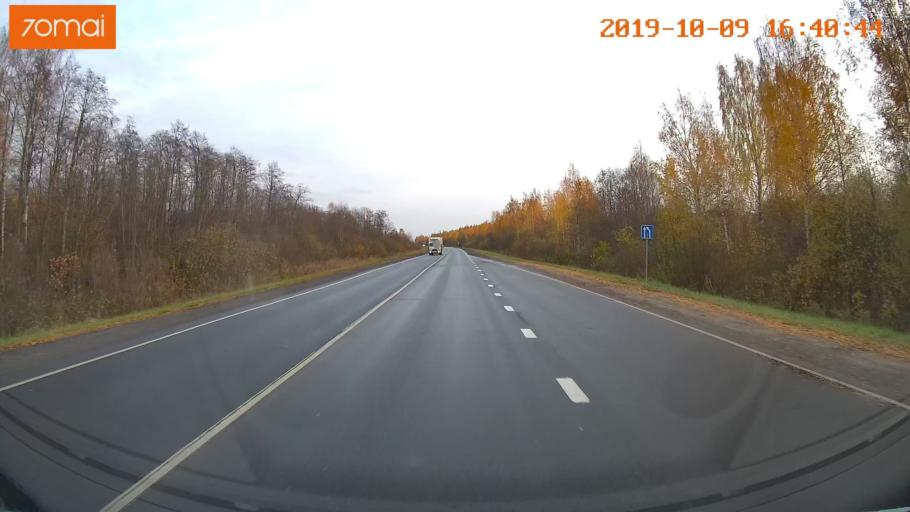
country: RU
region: Kostroma
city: Volgorechensk
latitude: 57.4800
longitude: 41.0661
